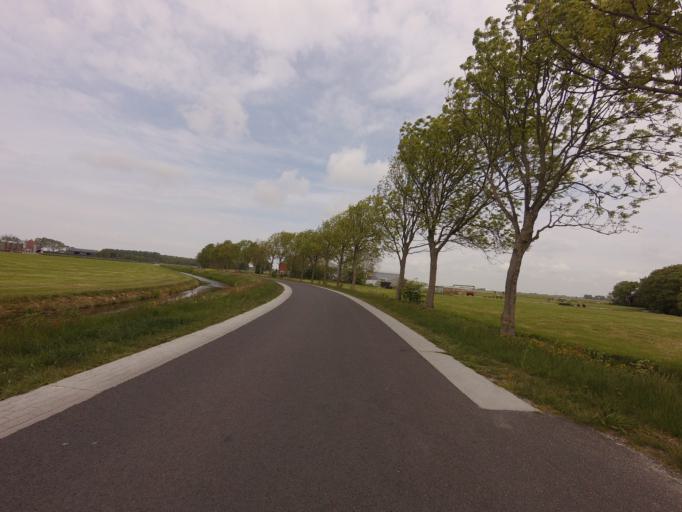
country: NL
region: Friesland
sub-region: Sudwest Fryslan
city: Bolsward
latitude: 53.0874
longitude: 5.4835
